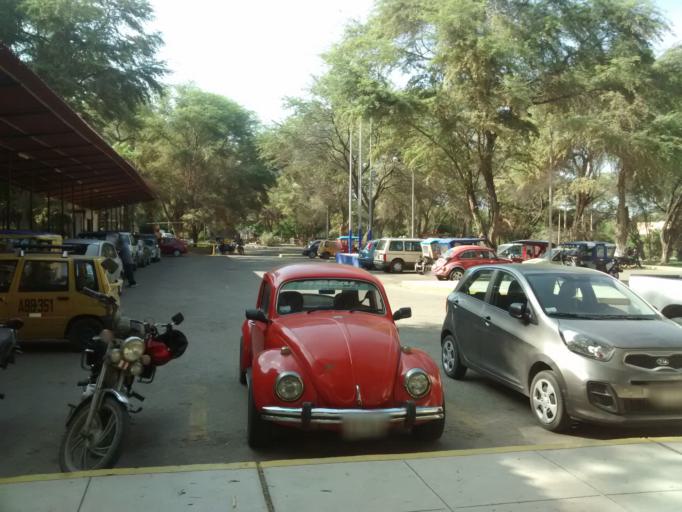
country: PE
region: Piura
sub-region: Provincia de Piura
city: Piura
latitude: -5.1790
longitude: -80.6188
